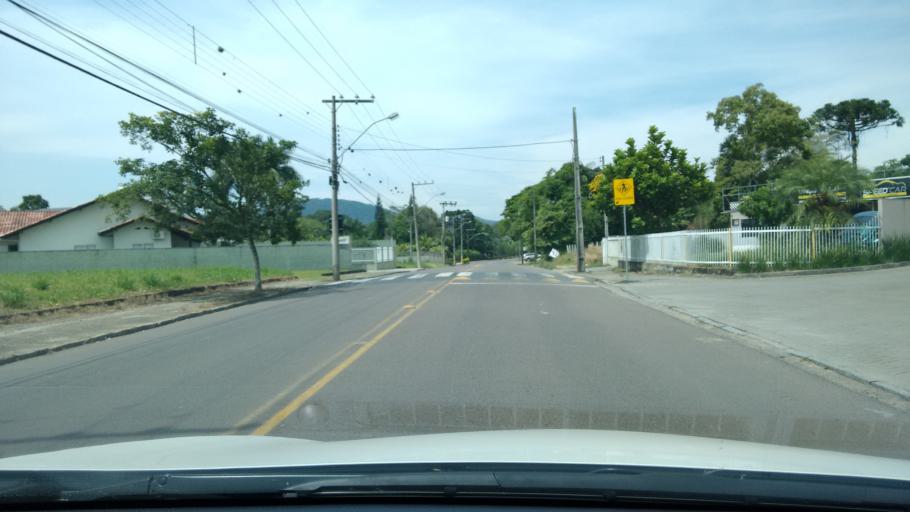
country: BR
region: Santa Catarina
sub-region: Timbo
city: Timbo
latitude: -26.8283
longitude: -49.2845
